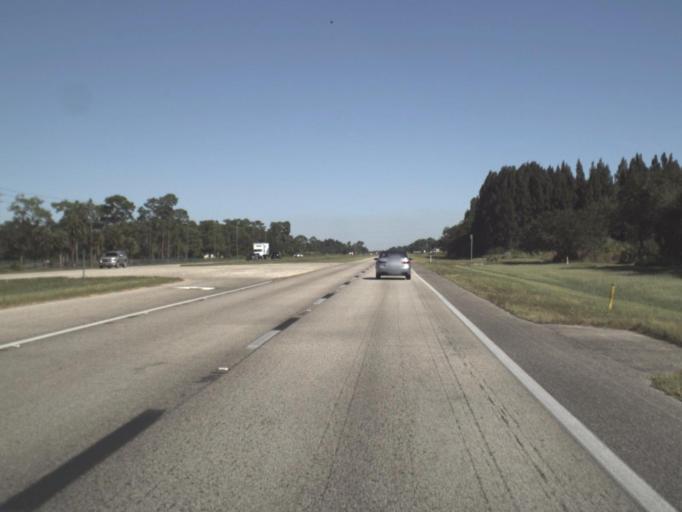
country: US
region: Florida
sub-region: Lee County
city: Alva
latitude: 26.7095
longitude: -81.5505
